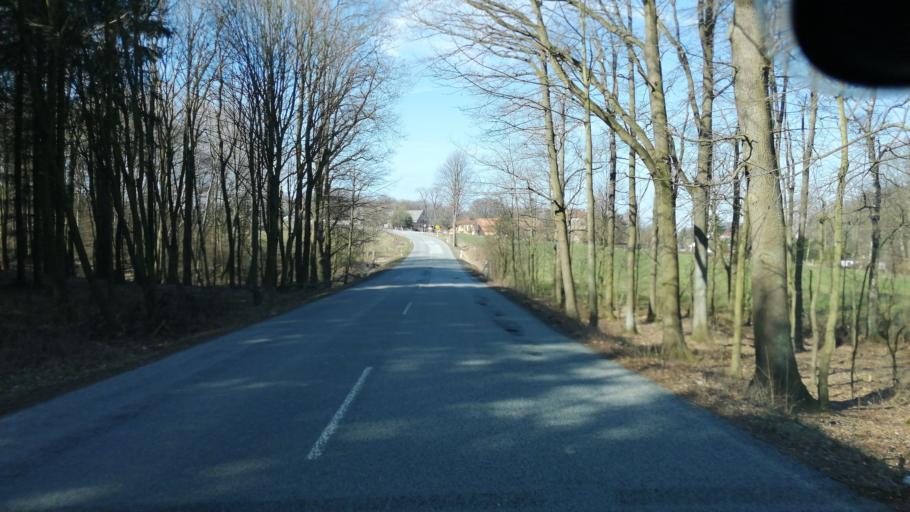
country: DE
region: Saxony
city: Schonbach
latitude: 51.0575
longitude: 14.5868
